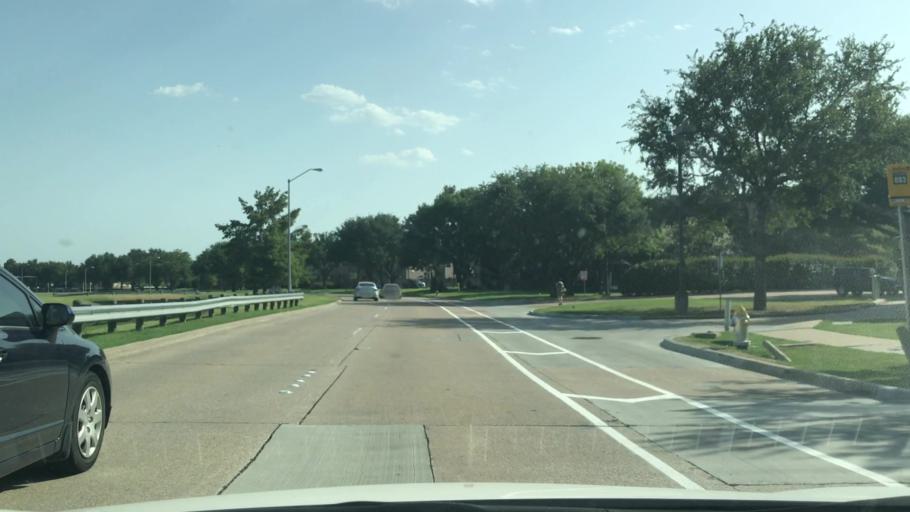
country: US
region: Texas
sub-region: Dallas County
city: Richardson
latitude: 32.9842
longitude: -96.7567
